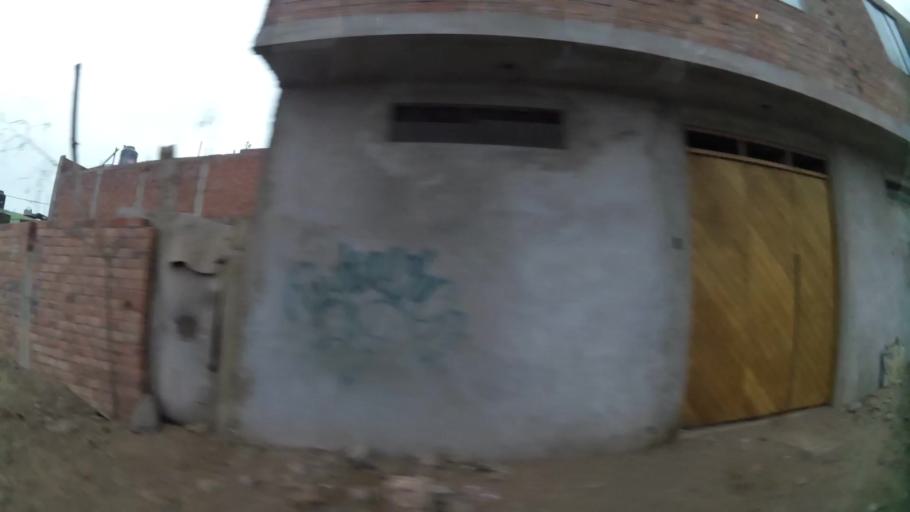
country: PE
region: Lima
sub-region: Lima
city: Surco
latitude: -12.1915
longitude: -77.0223
